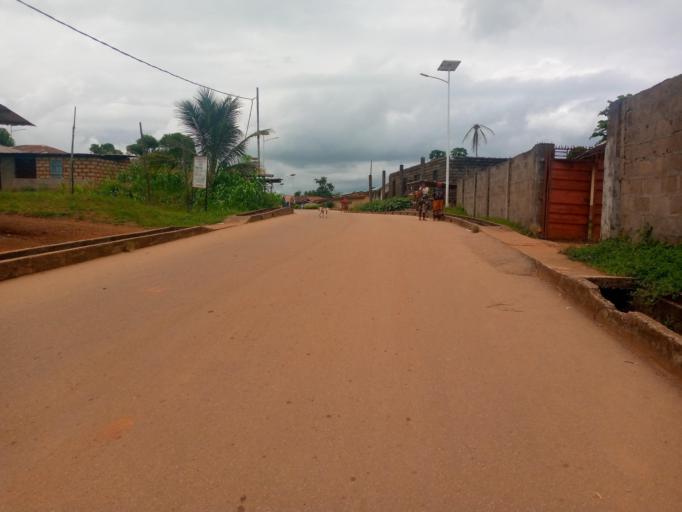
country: SL
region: Southern Province
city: Mogbwemo
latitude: 7.6072
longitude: -12.1806
